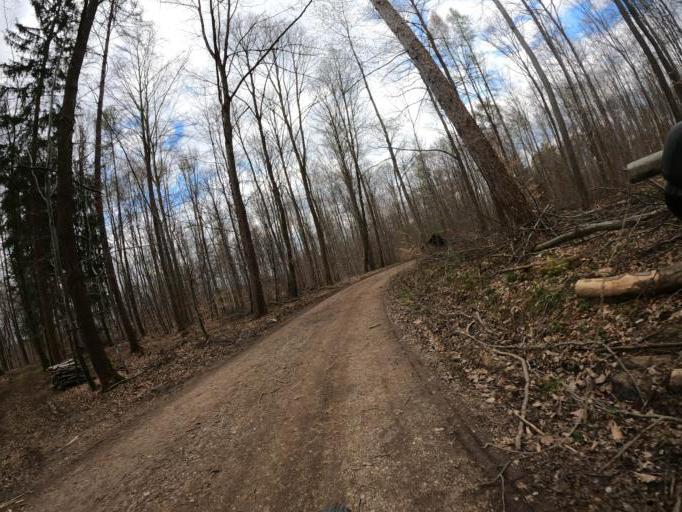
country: DE
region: Baden-Wuerttemberg
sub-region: Tuebingen Region
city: Gomaringen
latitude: 48.4488
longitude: 9.1220
